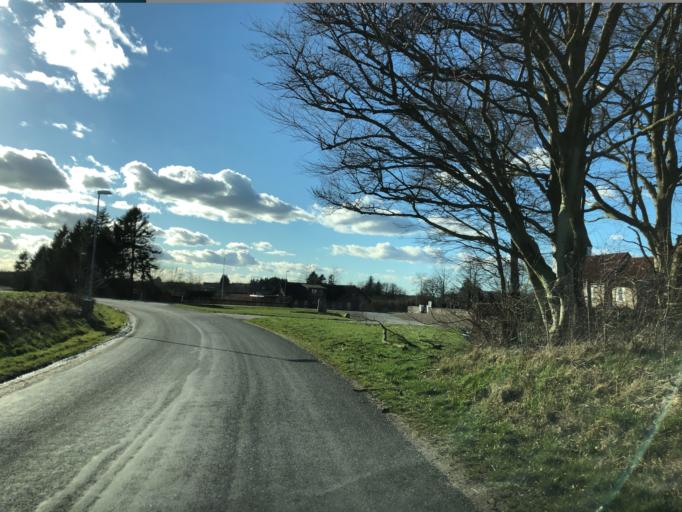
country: DK
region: Central Jutland
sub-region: Silkeborg Kommune
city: Kjellerup
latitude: 56.3326
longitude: 9.4856
